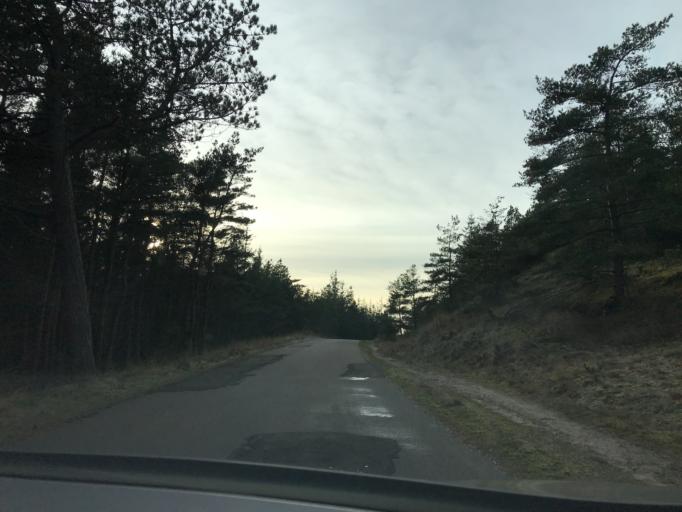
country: DK
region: South Denmark
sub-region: Varde Kommune
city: Oksbol
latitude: 55.7932
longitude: 8.2027
